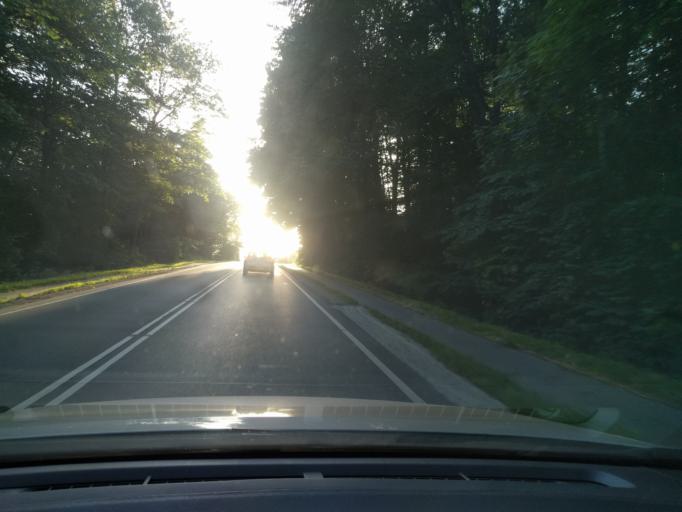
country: DK
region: Zealand
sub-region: Naestved Kommune
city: Naestved
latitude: 55.1856
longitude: 11.8576
